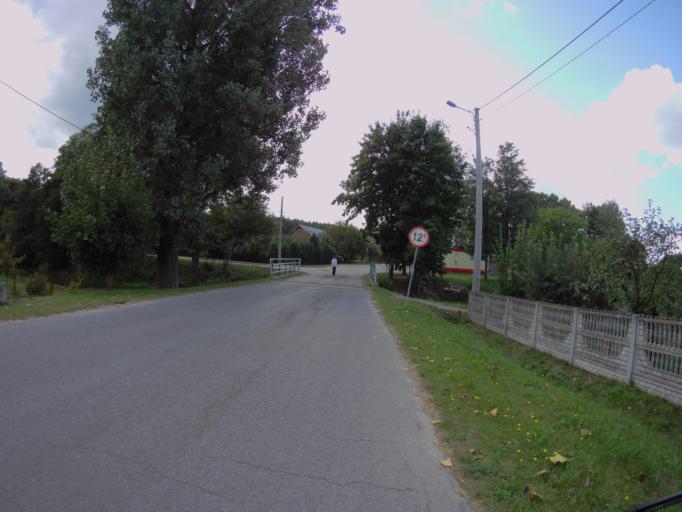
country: PL
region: Subcarpathian Voivodeship
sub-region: Powiat lezajski
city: Brzoza Krolewska
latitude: 50.2479
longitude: 22.3209
